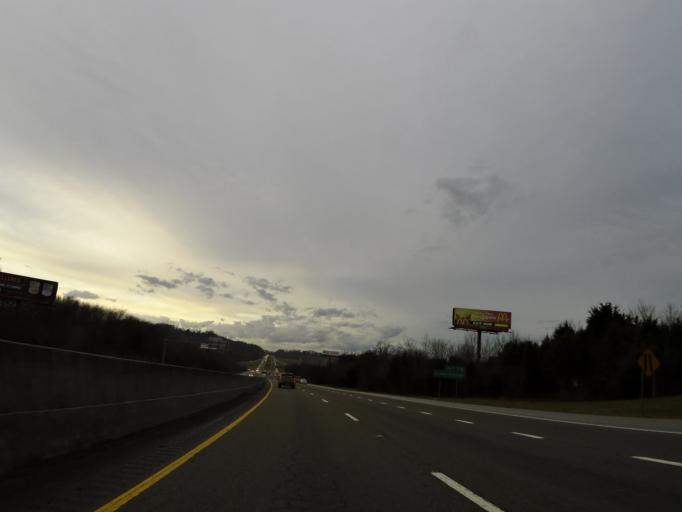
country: US
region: Tennessee
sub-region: Knox County
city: Knoxville
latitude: 36.0408
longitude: -83.9965
